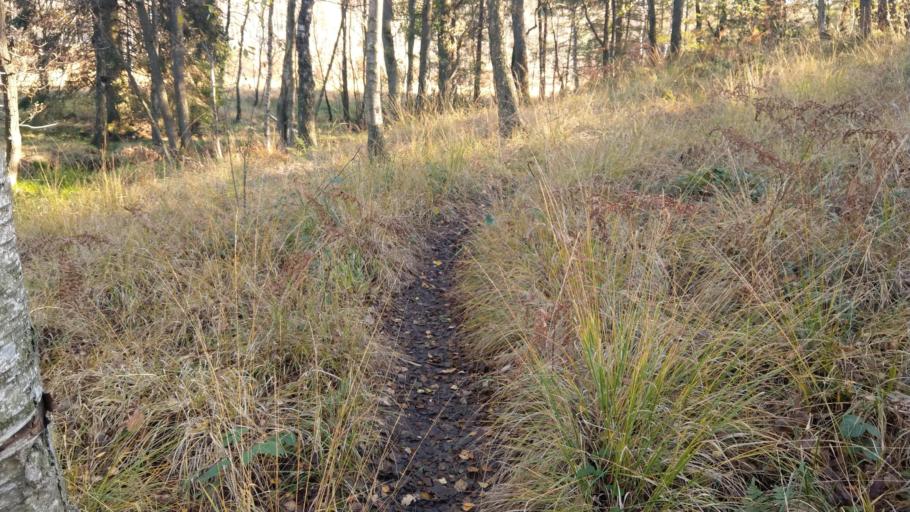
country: DE
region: North Rhine-Westphalia
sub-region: Regierungsbezirk Koln
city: Roetgen
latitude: 50.6710
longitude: 6.1626
